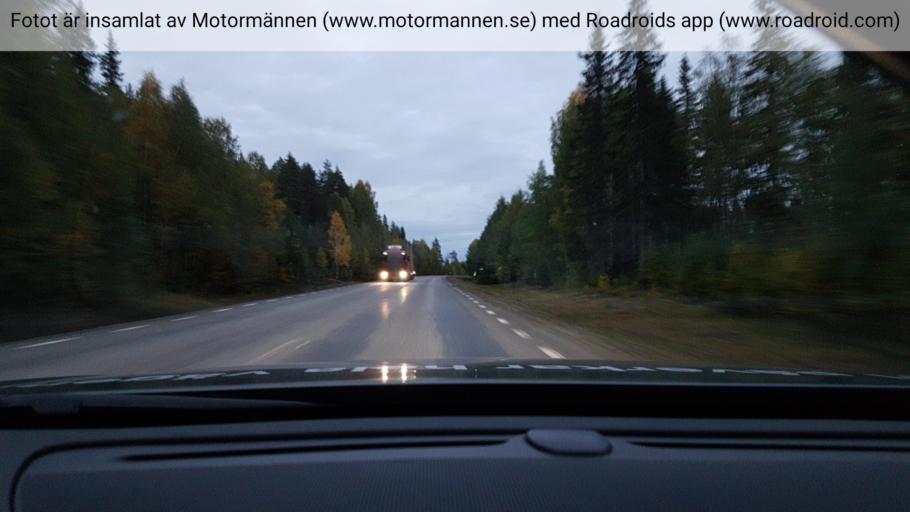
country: SE
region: Norrbotten
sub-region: Alvsbyns Kommun
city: AElvsbyn
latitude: 65.7785
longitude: 20.8342
